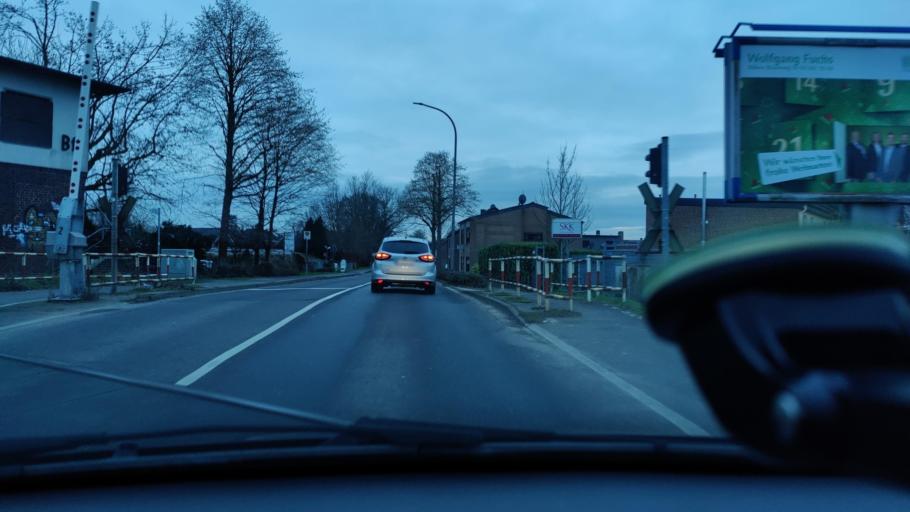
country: DE
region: North Rhine-Westphalia
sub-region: Regierungsbezirk Dusseldorf
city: Nettetal
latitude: 51.2755
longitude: 6.2723
